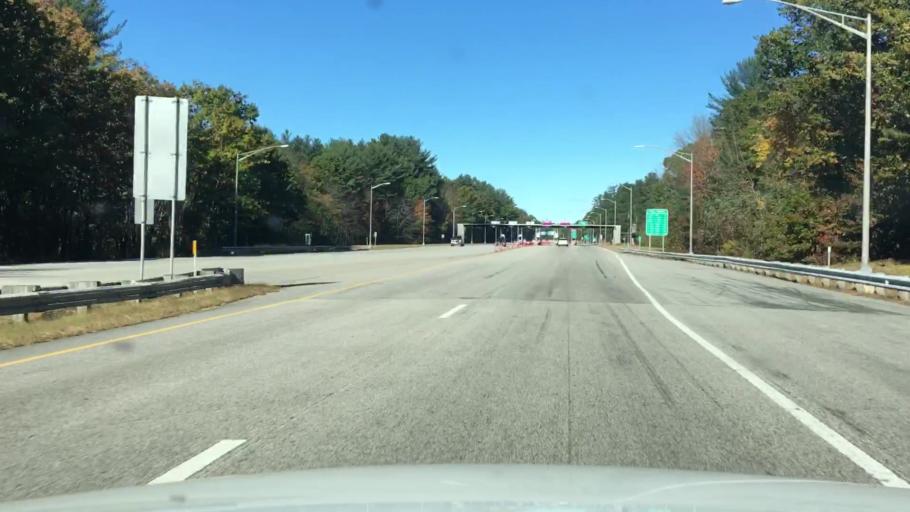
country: US
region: New Hampshire
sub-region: Strafford County
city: Rochester
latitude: 43.2720
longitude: -70.9611
